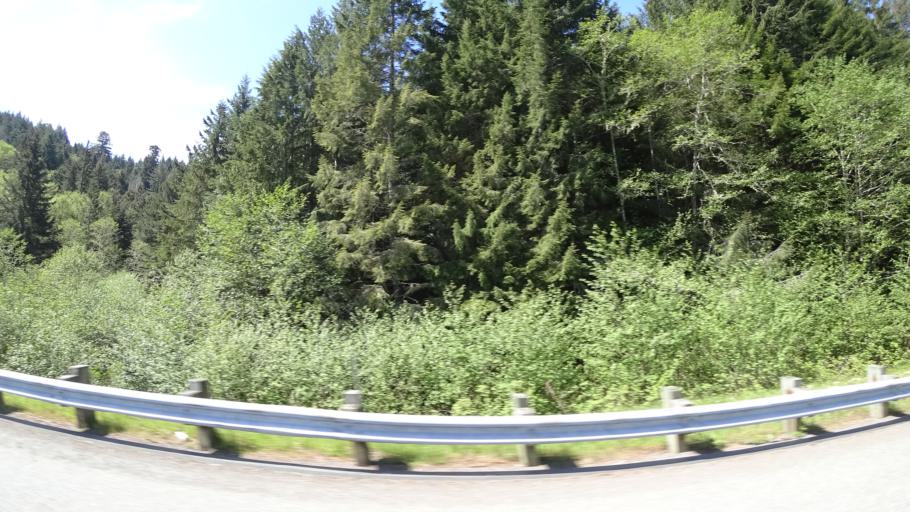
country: US
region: California
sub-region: Del Norte County
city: Bertsch-Oceanview
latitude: 41.4263
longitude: -124.0084
